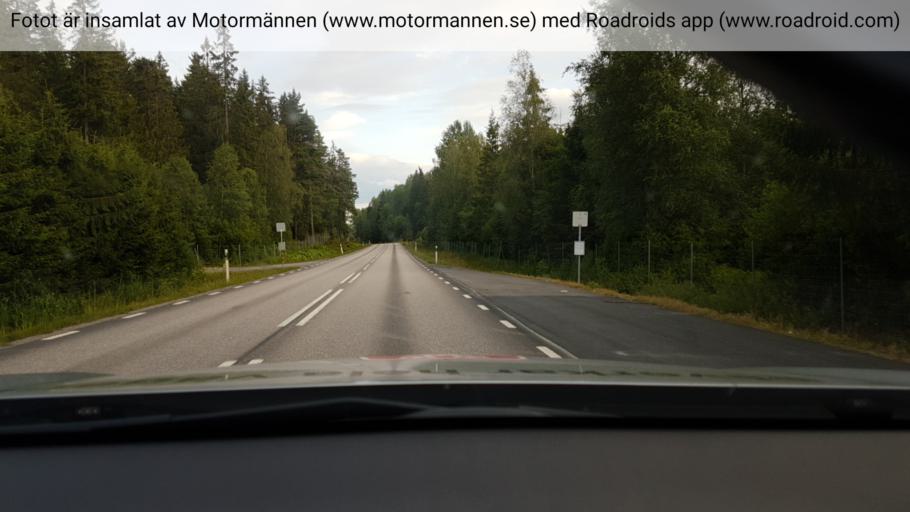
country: SE
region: Vaestra Goetaland
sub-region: Fargelanda Kommun
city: Faergelanda
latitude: 58.4719
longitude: 12.0160
